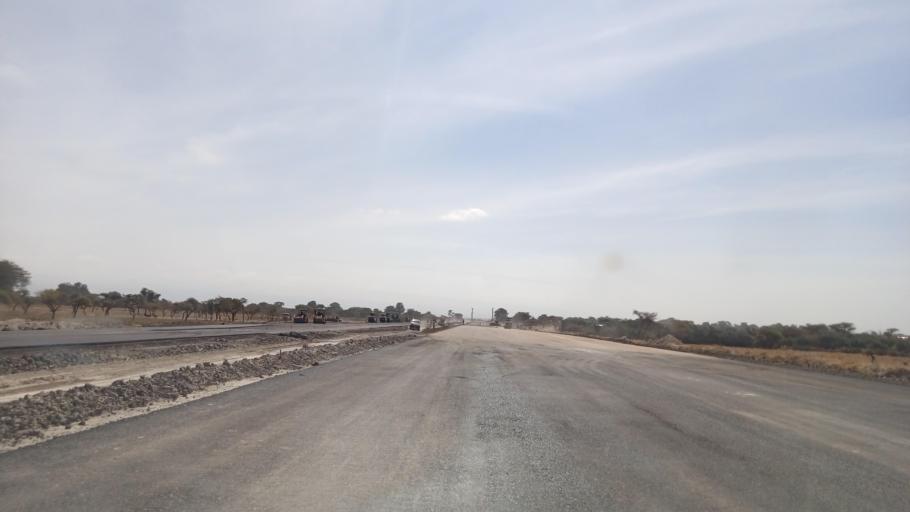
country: ET
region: Oromiya
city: Ziway
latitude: 7.7119
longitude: 38.6354
